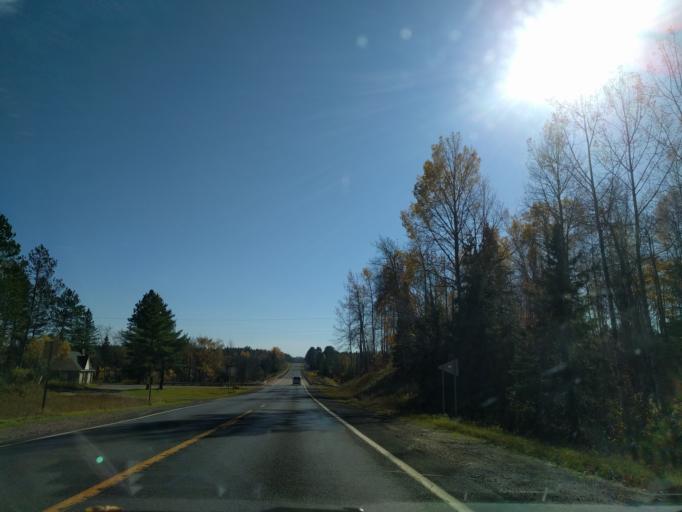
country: US
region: Michigan
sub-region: Iron County
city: Crystal Falls
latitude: 46.2497
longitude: -88.0109
